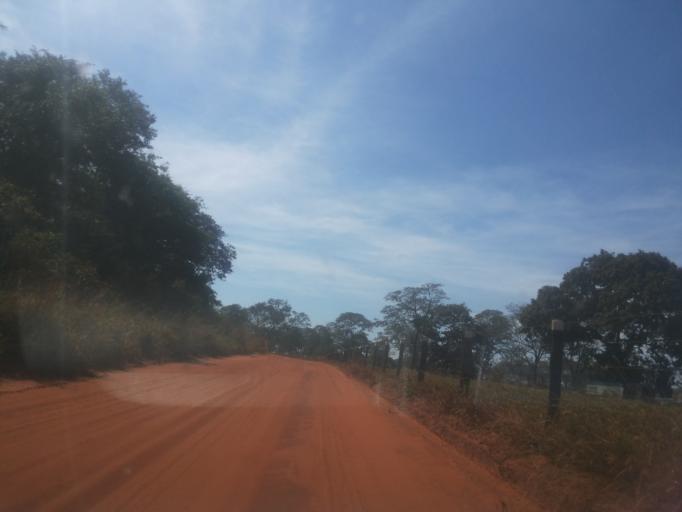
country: BR
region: Minas Gerais
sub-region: Santa Vitoria
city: Santa Vitoria
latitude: -19.0355
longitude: -50.4232
